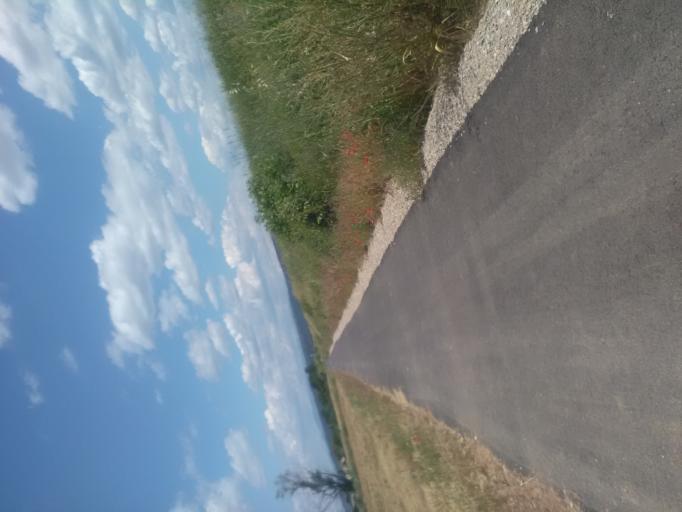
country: FR
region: Provence-Alpes-Cote d'Azur
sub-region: Departement des Alpes-de-Haute-Provence
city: Manosque
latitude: 43.8256
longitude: 5.8065
